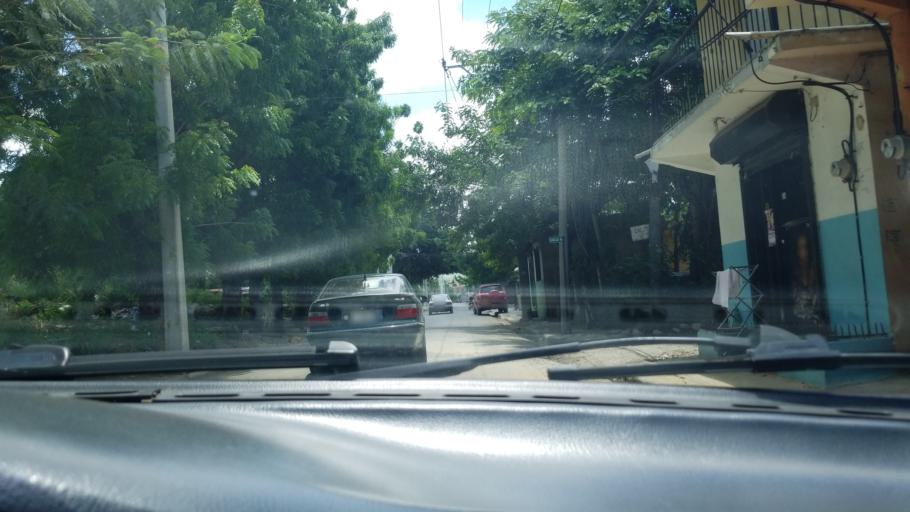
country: DO
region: Santiago
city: Santiago de los Caballeros
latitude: 19.4823
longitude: -70.6806
